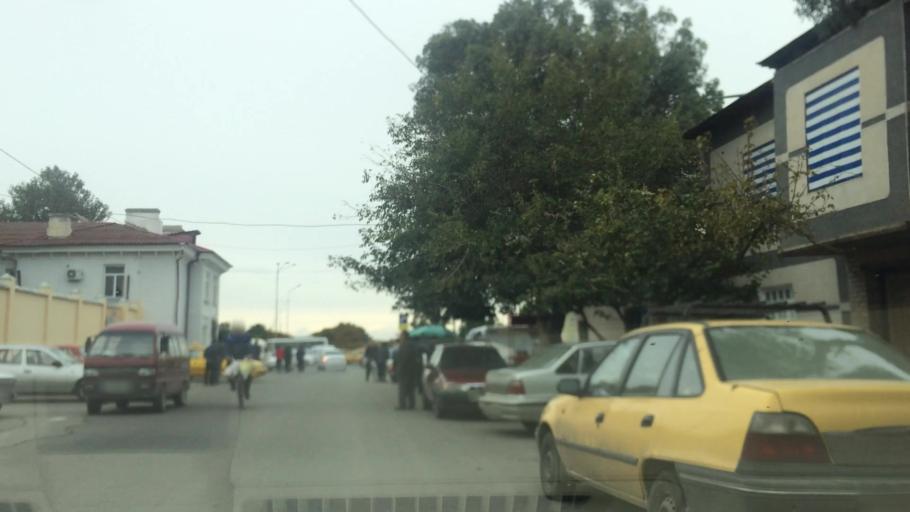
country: UZ
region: Samarqand
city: Samarqand
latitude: 39.6527
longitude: 66.9777
